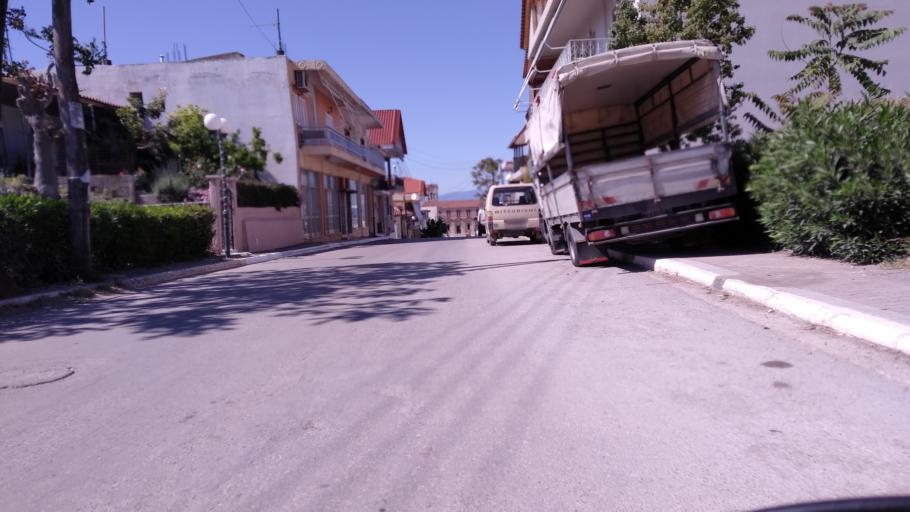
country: GR
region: Central Greece
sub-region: Nomos Fthiotidos
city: Malesina
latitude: 38.6209
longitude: 23.2319
